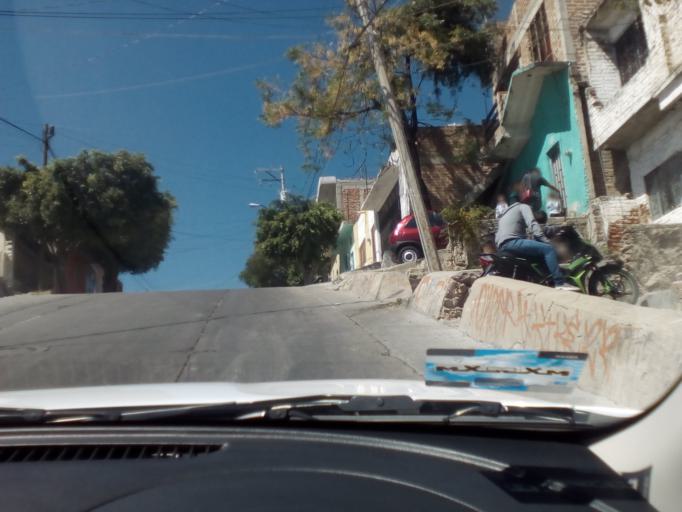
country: MX
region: Guanajuato
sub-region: Leon
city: Ejido la Joya
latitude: 21.1226
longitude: -101.7088
